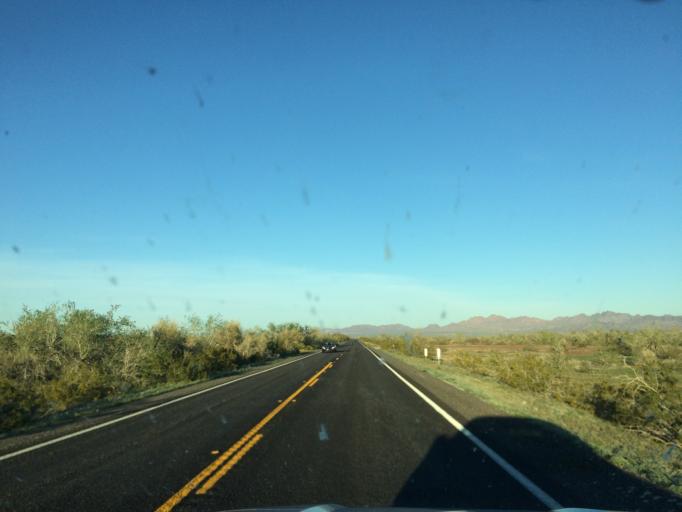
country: US
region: California
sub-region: Riverside County
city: Mesa Verde
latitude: 33.2845
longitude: -114.7735
